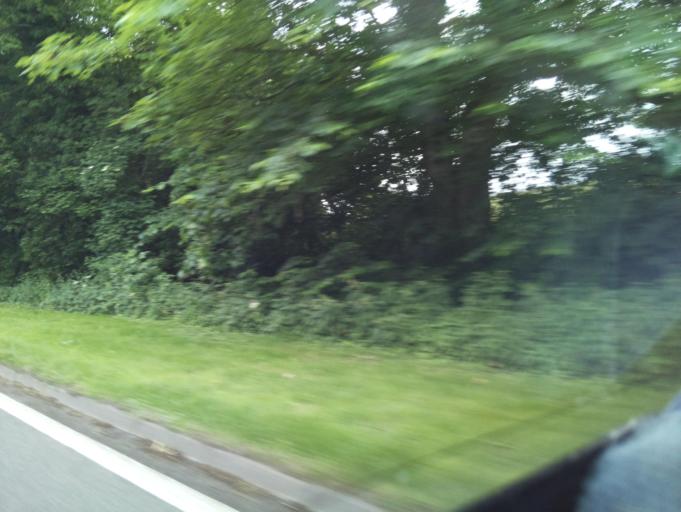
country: GB
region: England
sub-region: Derbyshire
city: Yeldersley
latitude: 52.9736
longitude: -1.6329
